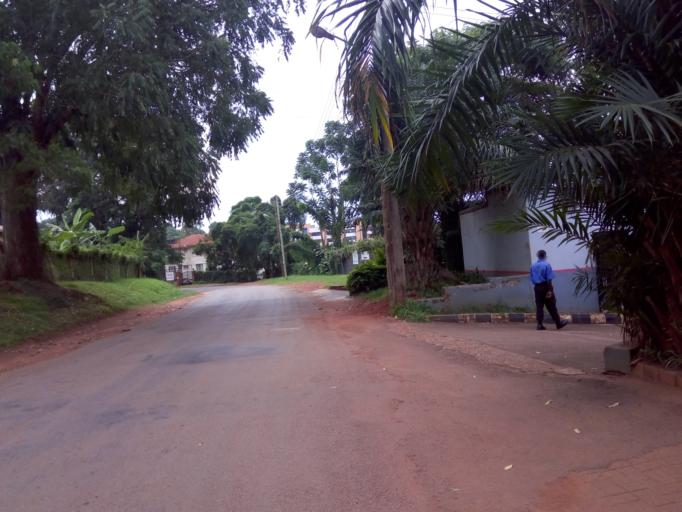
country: UG
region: Central Region
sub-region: Kampala District
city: Kampala
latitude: 0.3218
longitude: 32.5835
